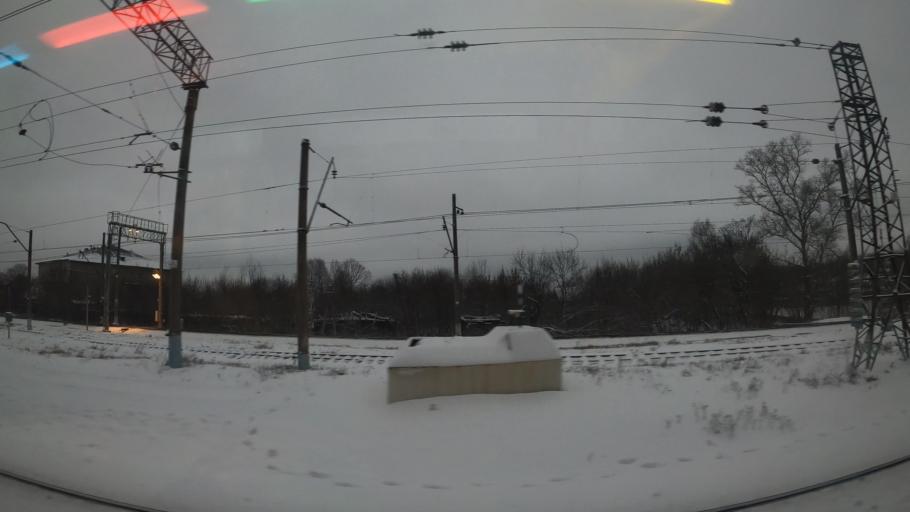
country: RU
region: Vladimir
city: Aleksandrov
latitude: 56.4038
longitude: 38.7123
